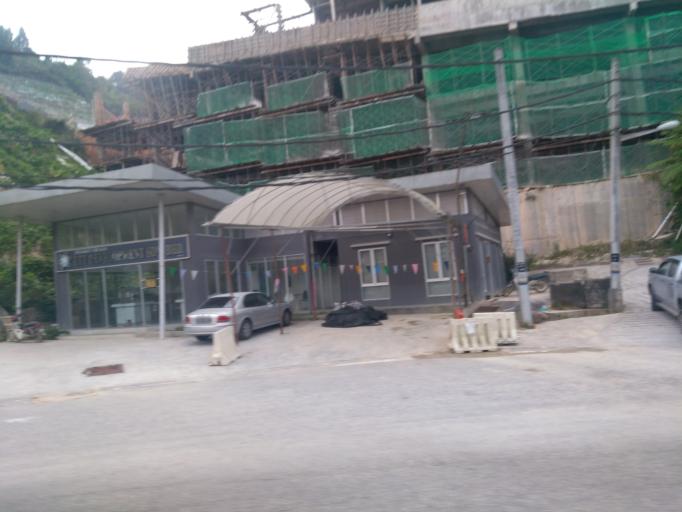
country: MY
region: Pahang
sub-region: Cameron Highlands
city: Tanah Rata
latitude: 4.5082
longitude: 101.4074
